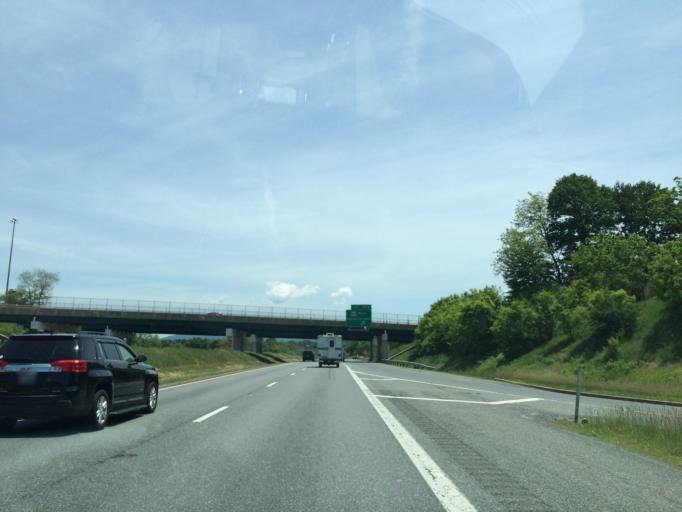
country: US
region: Maryland
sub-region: Washington County
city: Robinwood
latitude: 39.5997
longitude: -77.6841
